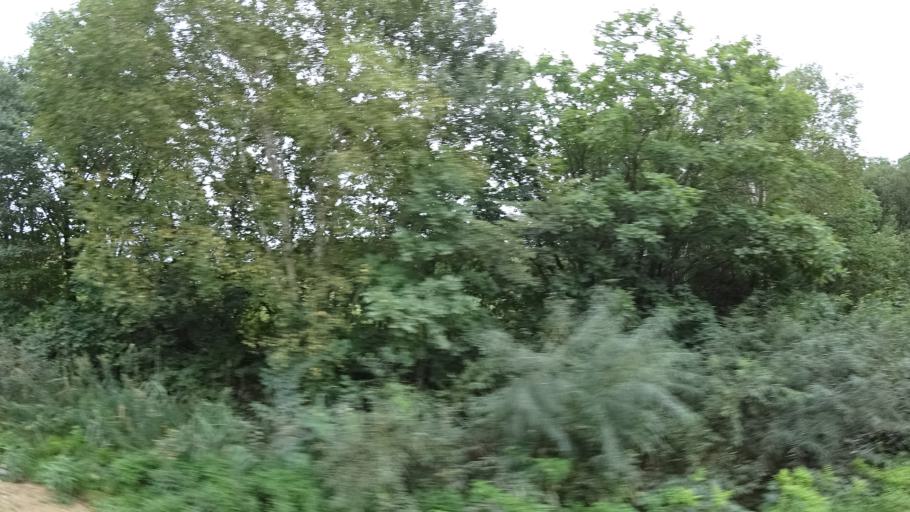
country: RU
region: Primorskiy
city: Rettikhovka
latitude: 44.1588
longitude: 132.6867
